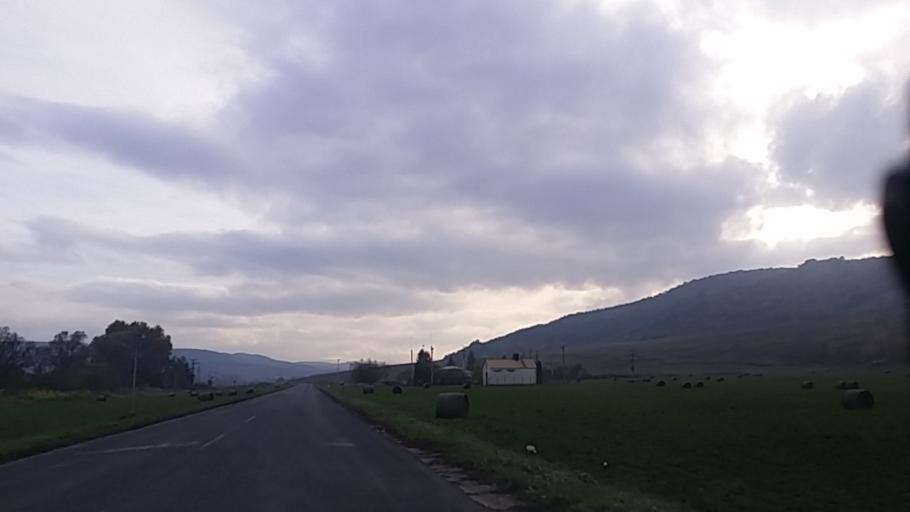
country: HU
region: Borsod-Abauj-Zemplen
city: Sajokaza
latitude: 48.2690
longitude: 20.5438
